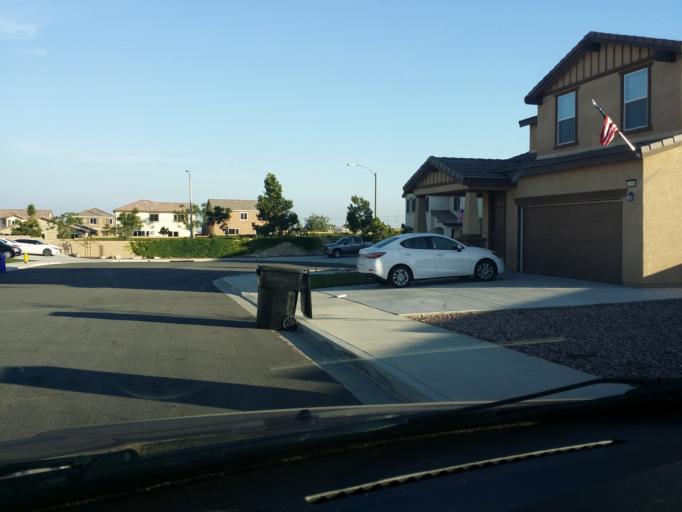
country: US
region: California
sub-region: San Bernardino County
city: Muscoy
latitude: 34.1895
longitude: -117.4216
